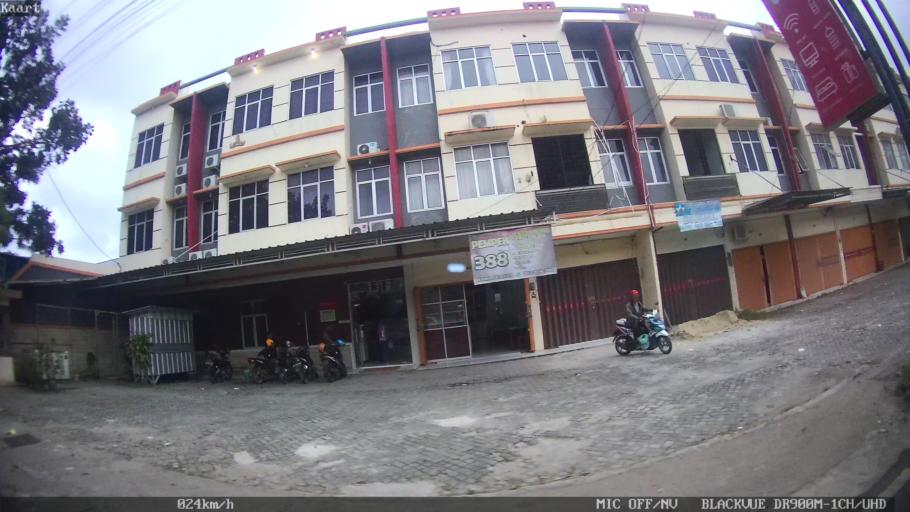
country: ID
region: Lampung
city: Bandarlampung
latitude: -5.4120
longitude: 105.2781
